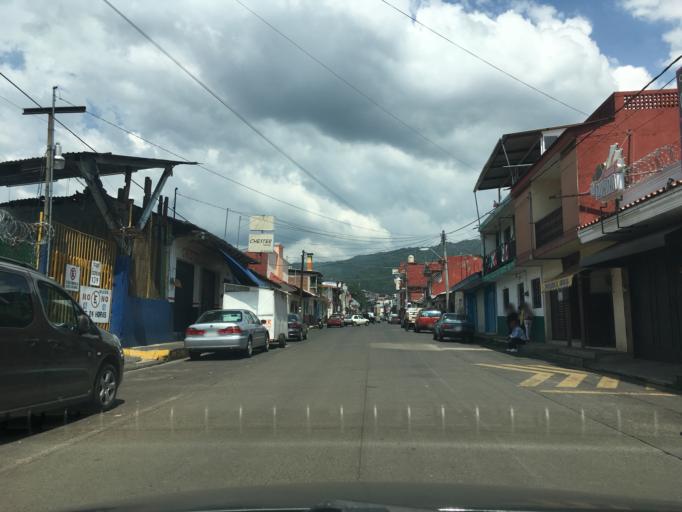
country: MX
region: Michoacan
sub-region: Uruapan
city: Uruapan
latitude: 19.4221
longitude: -102.0547
